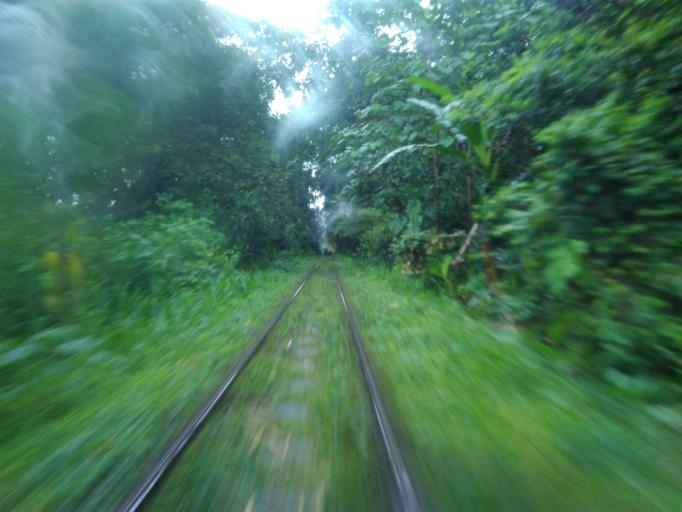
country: CO
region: Valle del Cauca
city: Buenaventura
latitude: 3.8475
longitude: -76.8628
